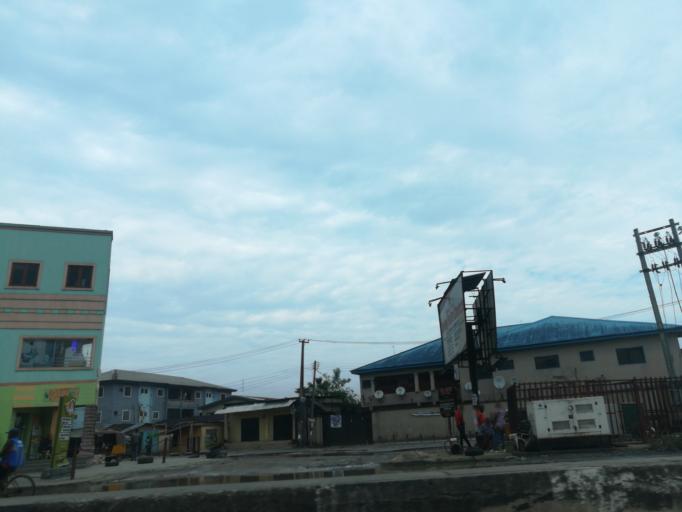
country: NG
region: Rivers
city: Port Harcourt
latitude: 4.8491
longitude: 6.9740
